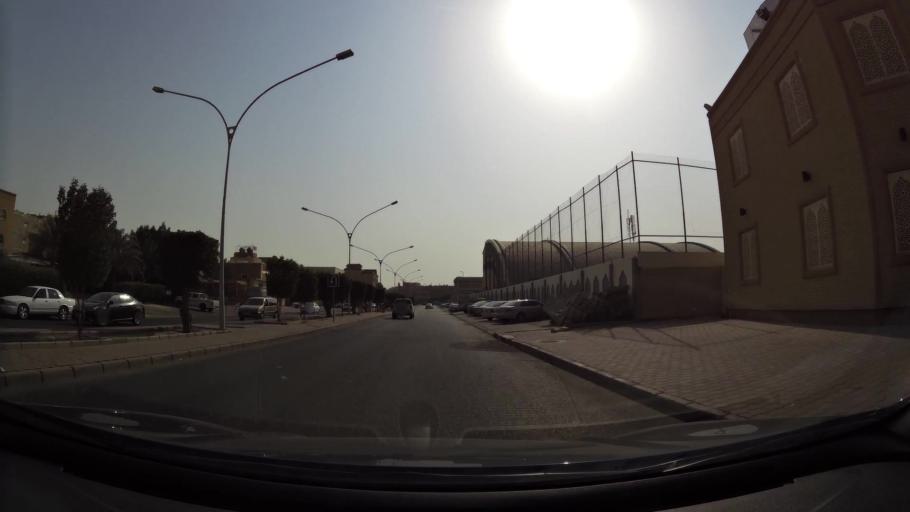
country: KW
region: Muhafazat al Jahra'
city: Al Jahra'
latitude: 29.3374
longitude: 47.7006
